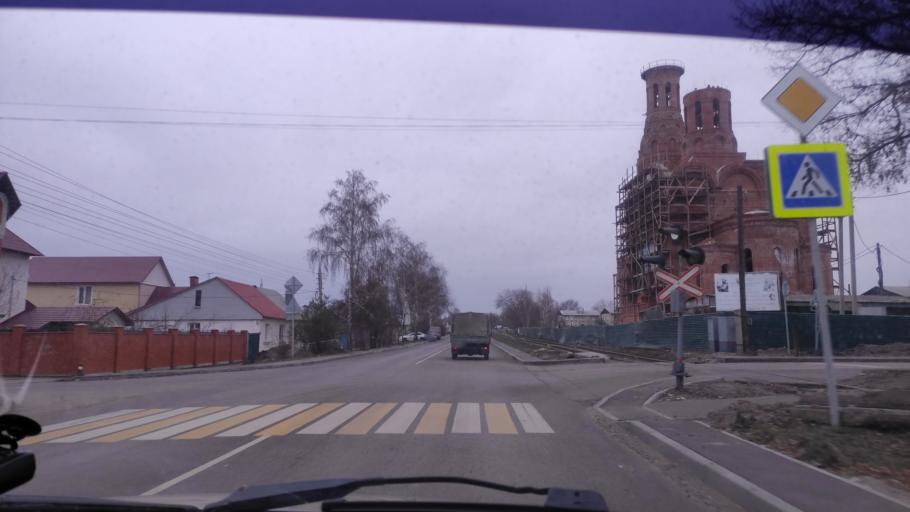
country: RU
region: Tambov
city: Tambov
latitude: 52.7211
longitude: 41.4113
